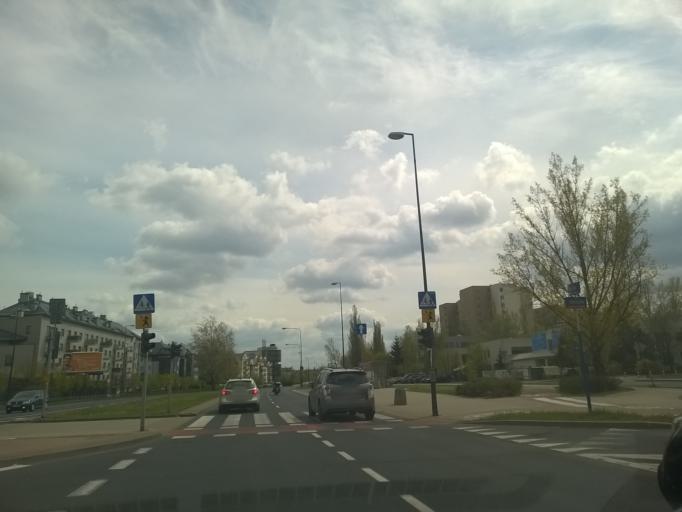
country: PL
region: Masovian Voivodeship
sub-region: Warszawa
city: Ursynow
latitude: 52.1523
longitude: 21.0565
